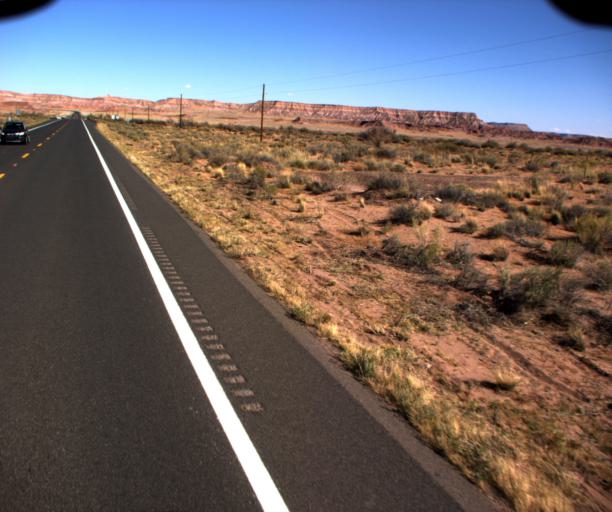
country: US
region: Arizona
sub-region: Coconino County
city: Tuba City
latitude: 36.0776
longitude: -111.3837
